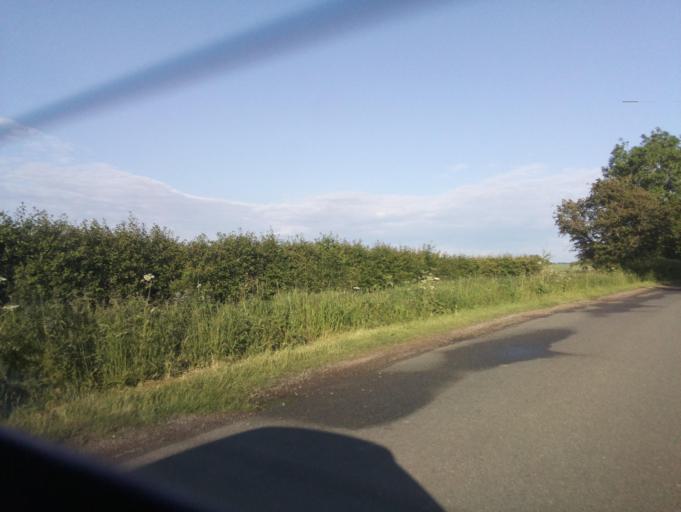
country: GB
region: England
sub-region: Lincolnshire
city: Navenby
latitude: 53.1170
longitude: -0.6229
